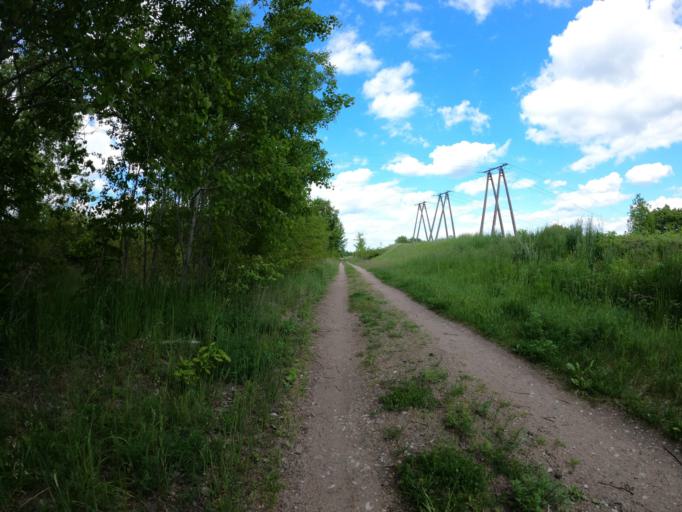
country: PL
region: Warmian-Masurian Voivodeship
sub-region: Powiat lidzbarski
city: Lidzbark Warminski
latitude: 54.1379
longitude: 20.5980
